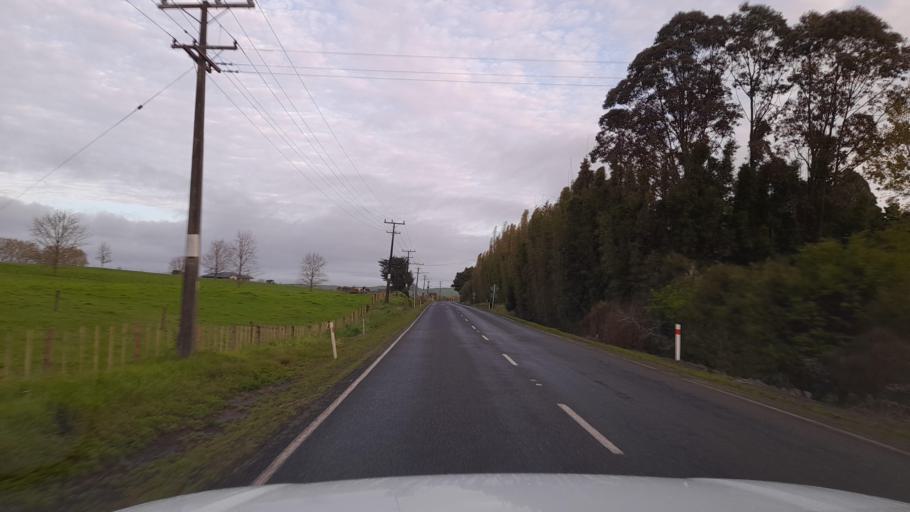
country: NZ
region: Northland
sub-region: Whangarei
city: Maungatapere
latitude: -35.7375
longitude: 174.1279
